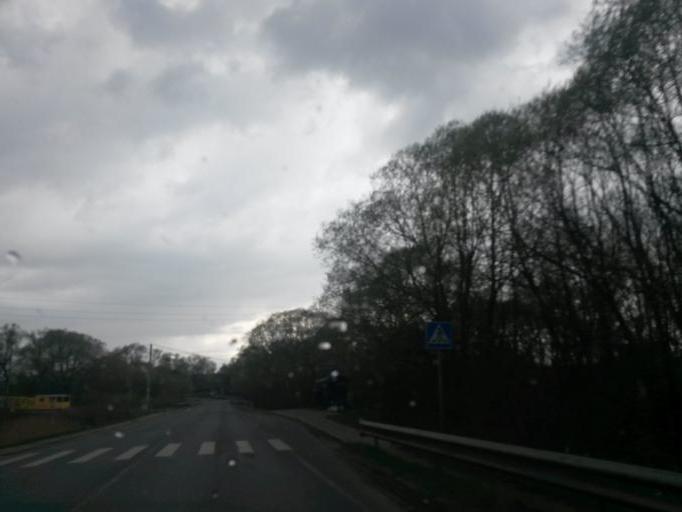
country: RU
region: Moskovskaya
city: Lyubuchany
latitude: 55.2491
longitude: 37.5493
